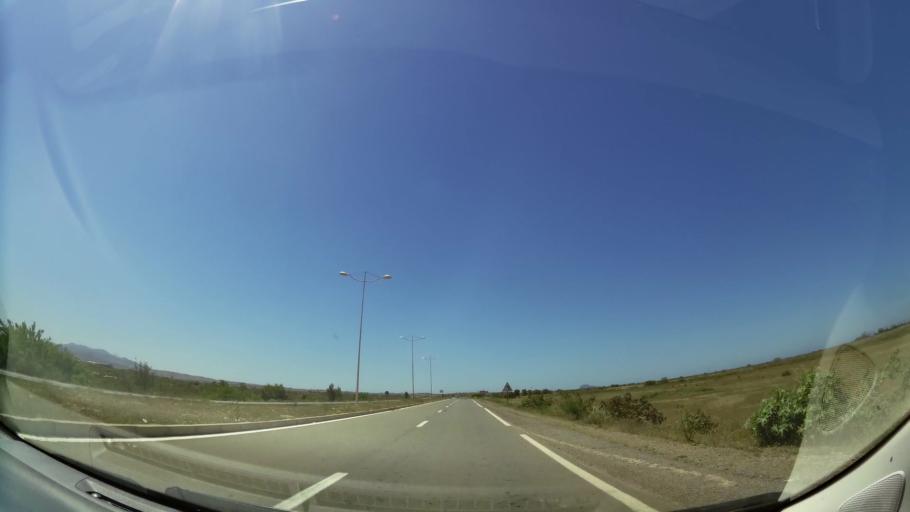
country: MA
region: Oriental
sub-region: Berkane-Taourirt
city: Madagh
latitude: 35.1040
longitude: -2.3422
